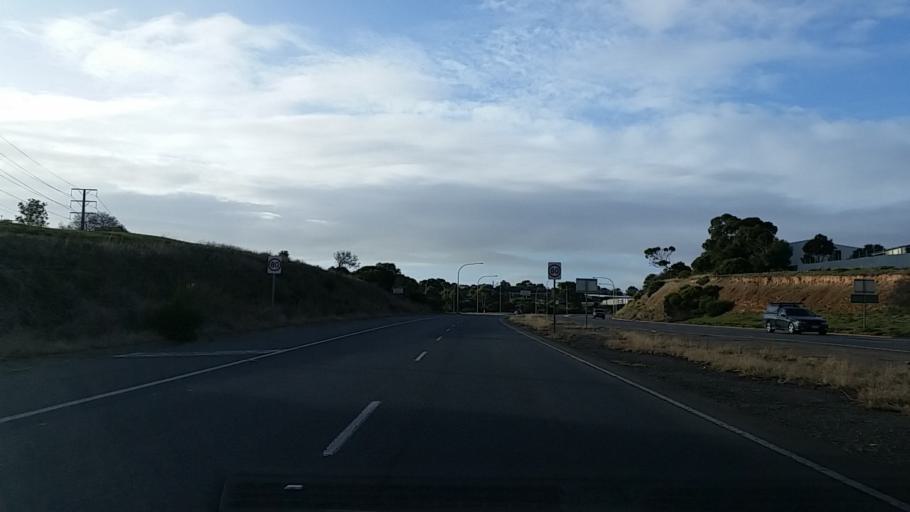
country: AU
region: South Australia
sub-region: Onkaparinga
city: Morphett Vale
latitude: -35.1153
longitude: 138.4911
